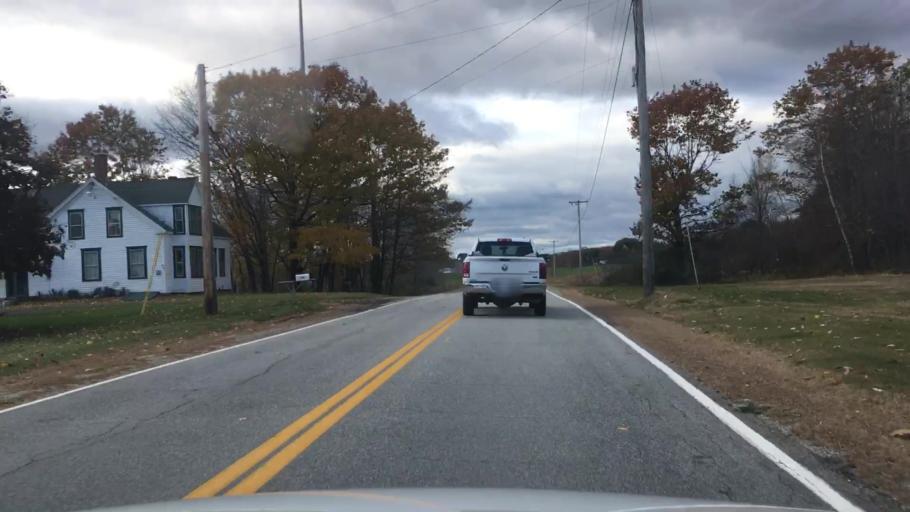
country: US
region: Maine
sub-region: Androscoggin County
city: Leeds
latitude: 44.3318
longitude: -70.1254
